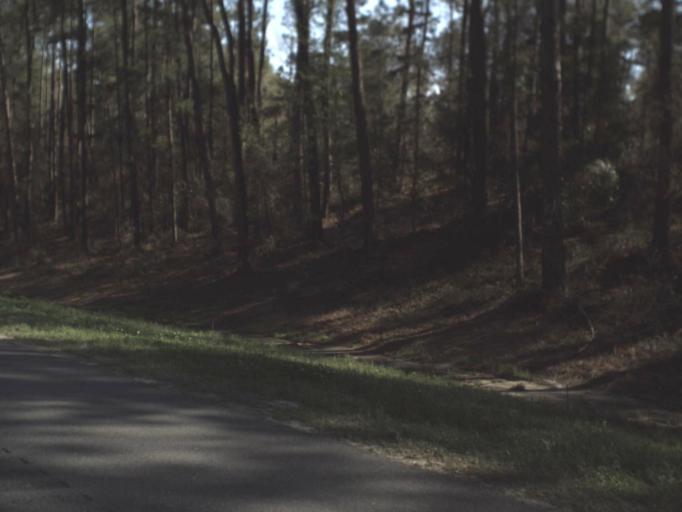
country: US
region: Florida
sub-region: Gadsden County
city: Midway
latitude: 30.5207
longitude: -84.4899
